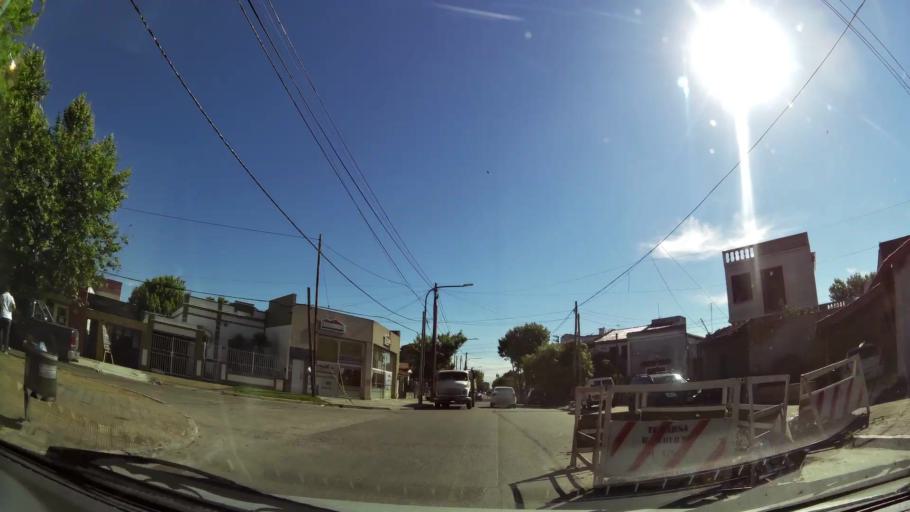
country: AR
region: Buenos Aires
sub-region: Partido de Lomas de Zamora
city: Lomas de Zamora
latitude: -34.7670
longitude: -58.4077
